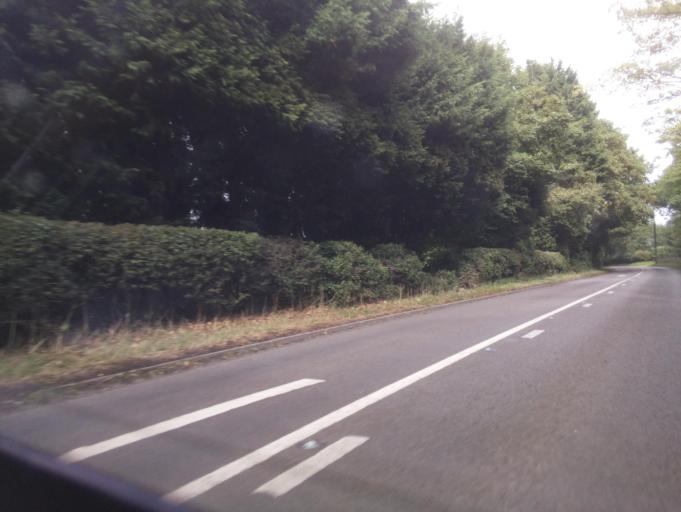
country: GB
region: England
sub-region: Staffordshire
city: Eccleshall
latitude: 52.8399
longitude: -2.2639
